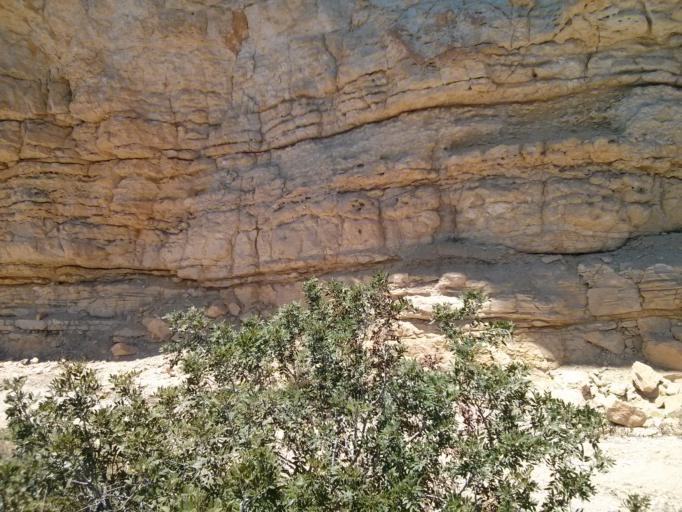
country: ES
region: Valencia
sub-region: Provincia de Alicante
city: Benitachell
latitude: 38.7101
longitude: 0.1652
